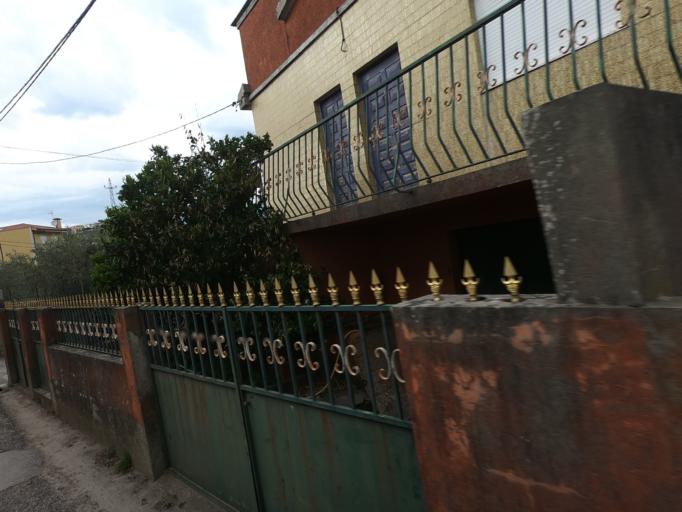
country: PT
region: Vila Real
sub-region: Sabrosa
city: Vilela
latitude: 41.2048
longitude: -7.6588
